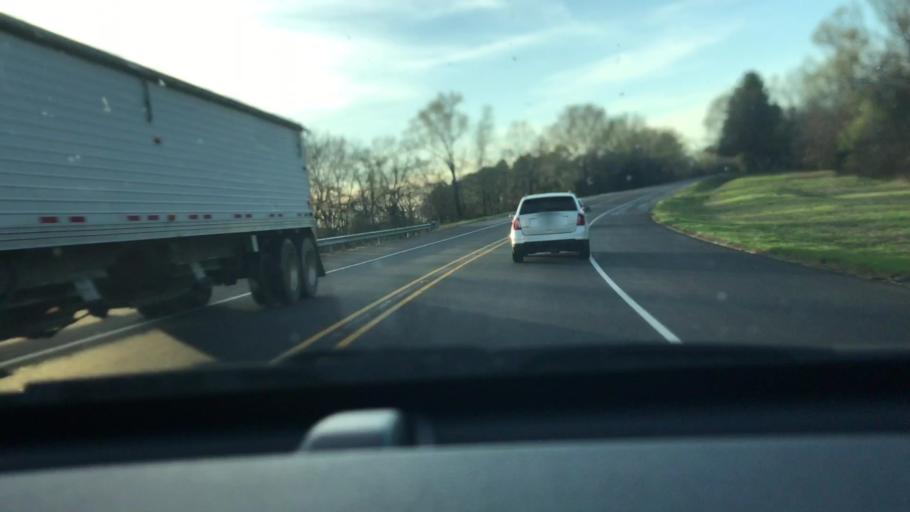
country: US
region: Texas
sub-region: Red River County
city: Clarksville
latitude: 33.5869
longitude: -94.9392
